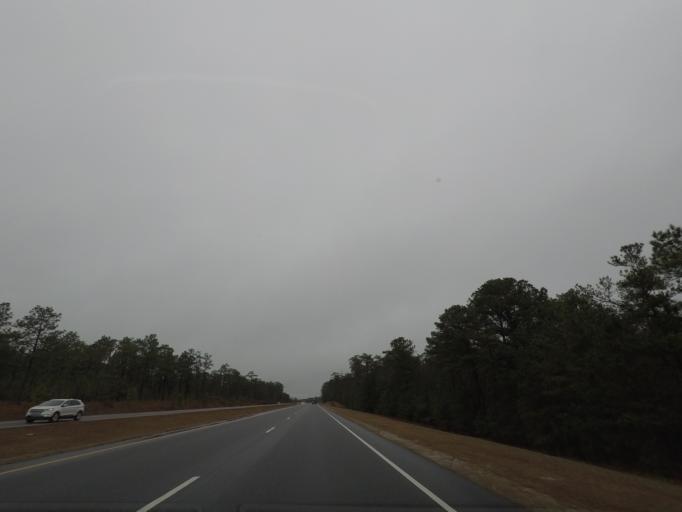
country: US
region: North Carolina
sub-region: Cumberland County
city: Spring Lake
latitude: 35.2376
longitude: -79.0205
